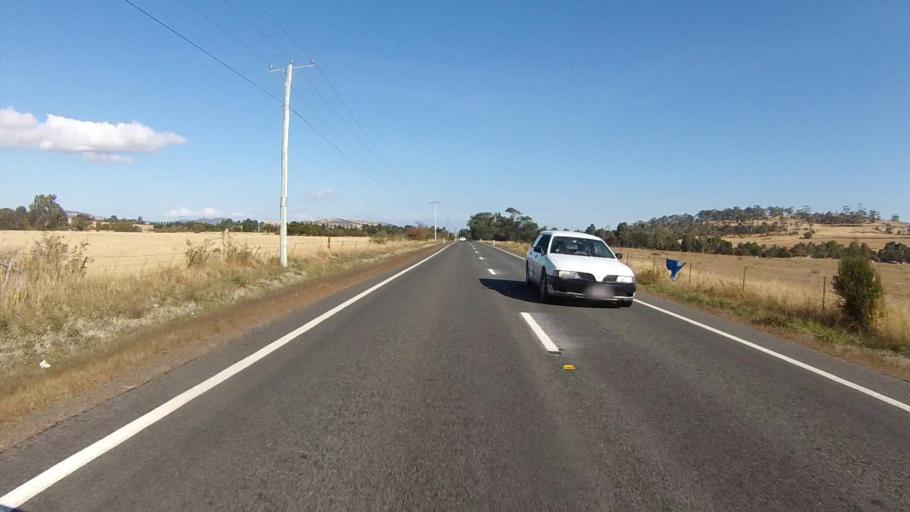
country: AU
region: Tasmania
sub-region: Sorell
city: Sorell
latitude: -42.7208
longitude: 147.5206
